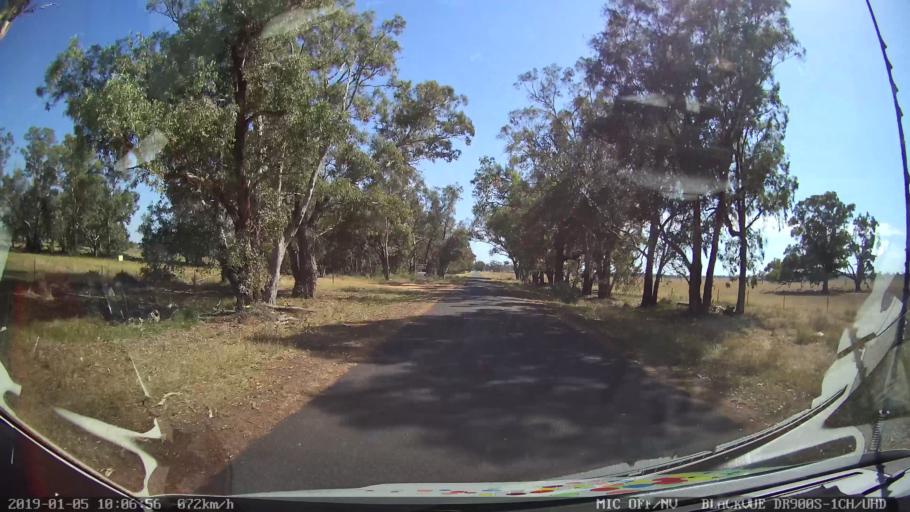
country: AU
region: New South Wales
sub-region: Gilgandra
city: Gilgandra
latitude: -31.6536
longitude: 148.8715
